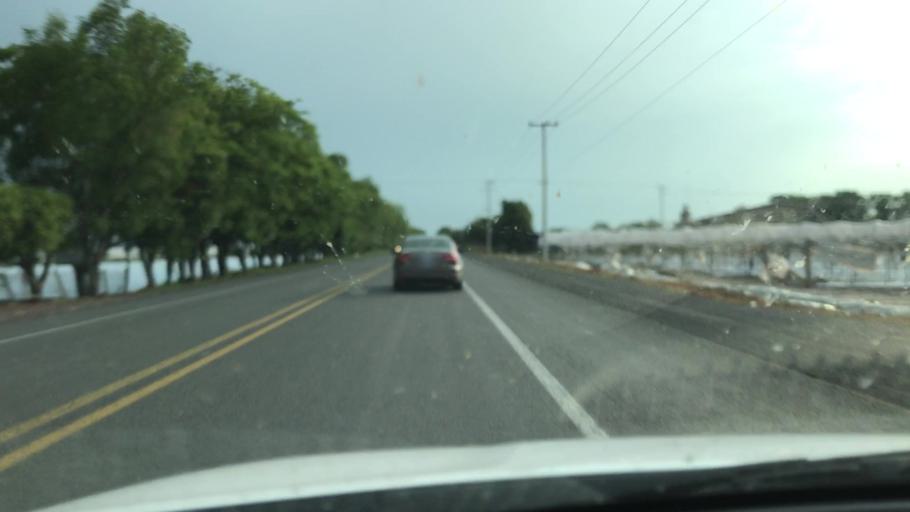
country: MX
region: Michoacan
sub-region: Yurecuaro
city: Yurecuaro
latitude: 20.3208
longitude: -102.2914
